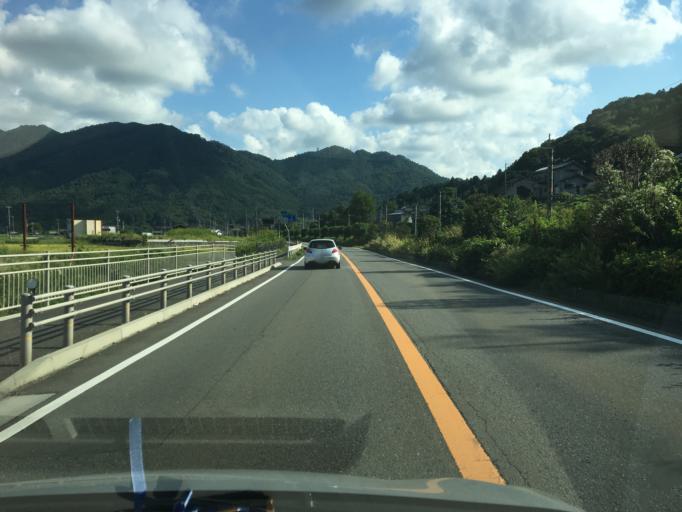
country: JP
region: Hyogo
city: Toyooka
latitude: 35.4286
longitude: 134.7876
